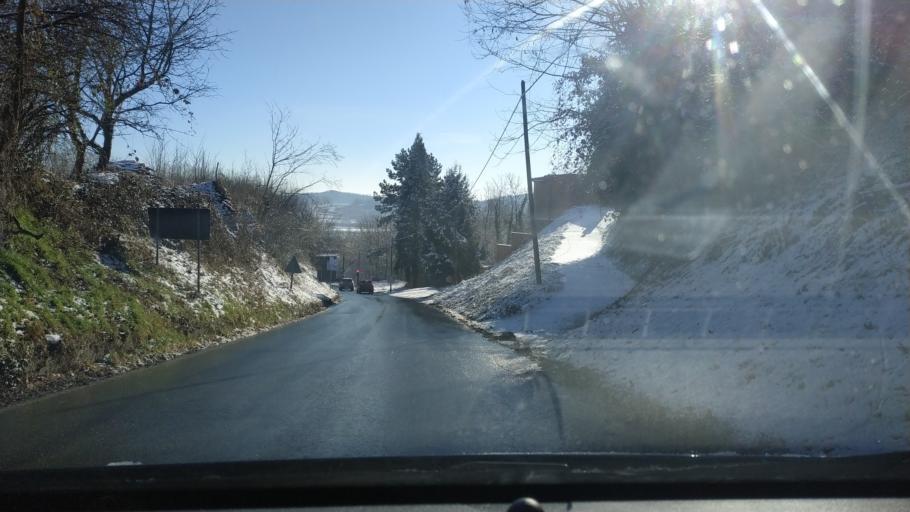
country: IT
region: Piedmont
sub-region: Provincia di Torino
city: Candia Canavese
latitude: 45.3262
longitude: 7.8896
